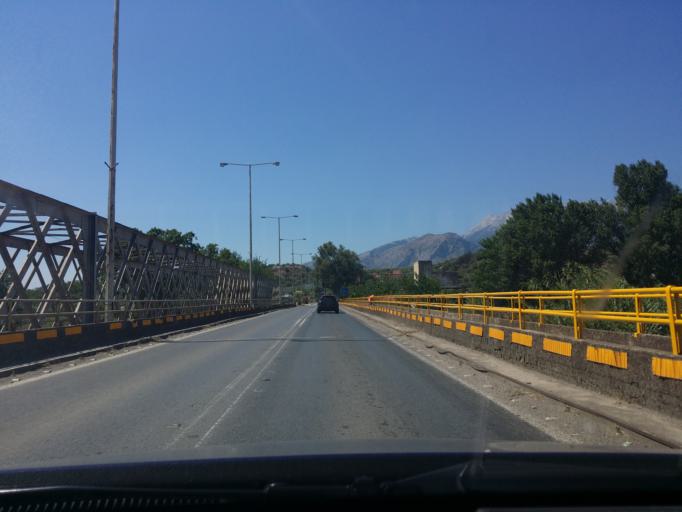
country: GR
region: Peloponnese
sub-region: Nomos Lakonias
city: Sparti
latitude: 37.0891
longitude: 22.4307
